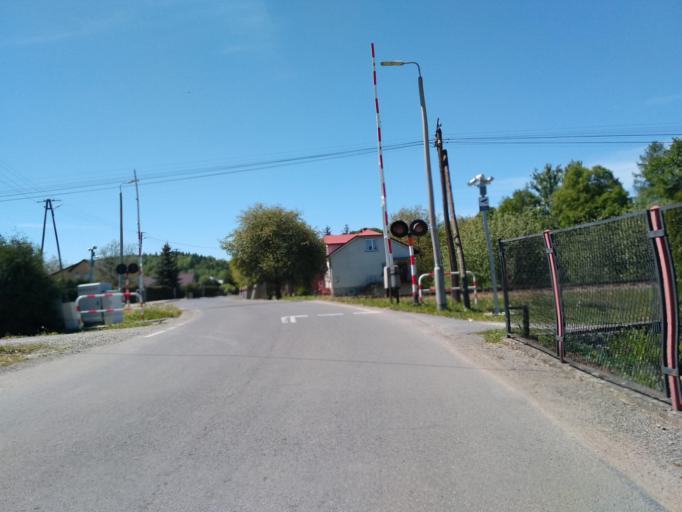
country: PL
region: Subcarpathian Voivodeship
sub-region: Powiat sanocki
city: Besko
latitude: 49.5896
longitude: 21.9591
